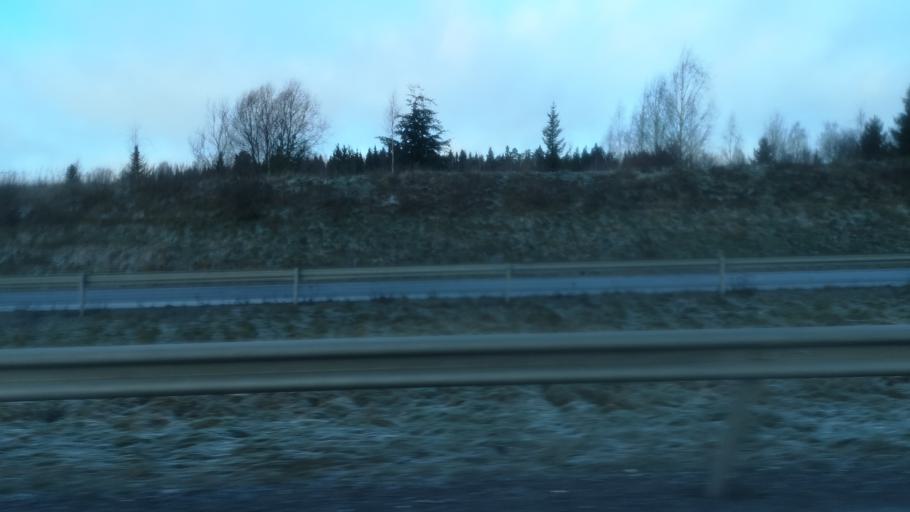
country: FI
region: Paijanne Tavastia
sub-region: Lahti
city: Lahti
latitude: 60.9462
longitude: 25.6808
